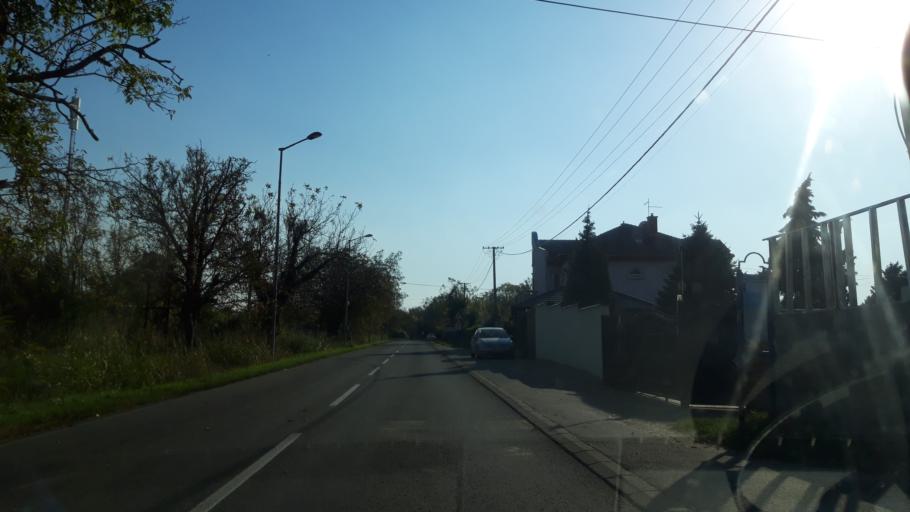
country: RS
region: Autonomna Pokrajina Vojvodina
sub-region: Juznobacki Okrug
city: Petrovaradin
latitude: 45.2399
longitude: 19.8664
